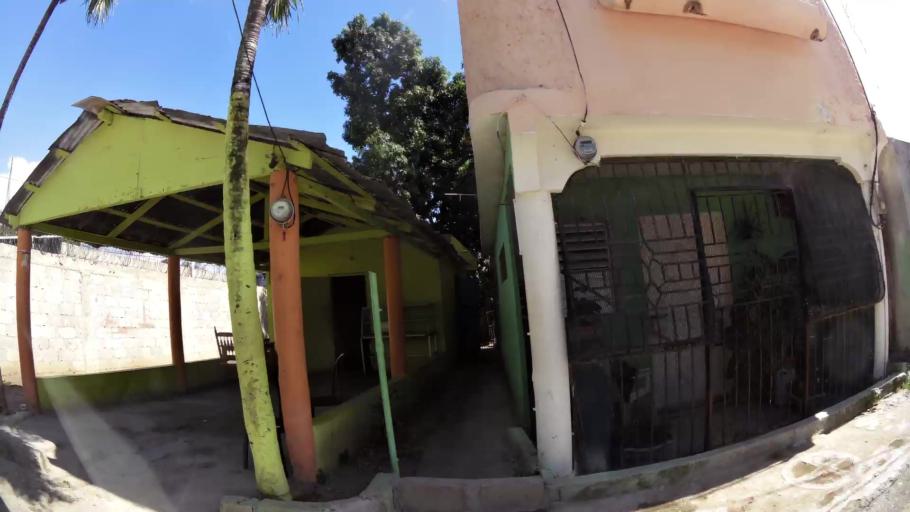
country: DO
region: San Cristobal
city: San Cristobal
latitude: 18.4232
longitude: -70.1007
